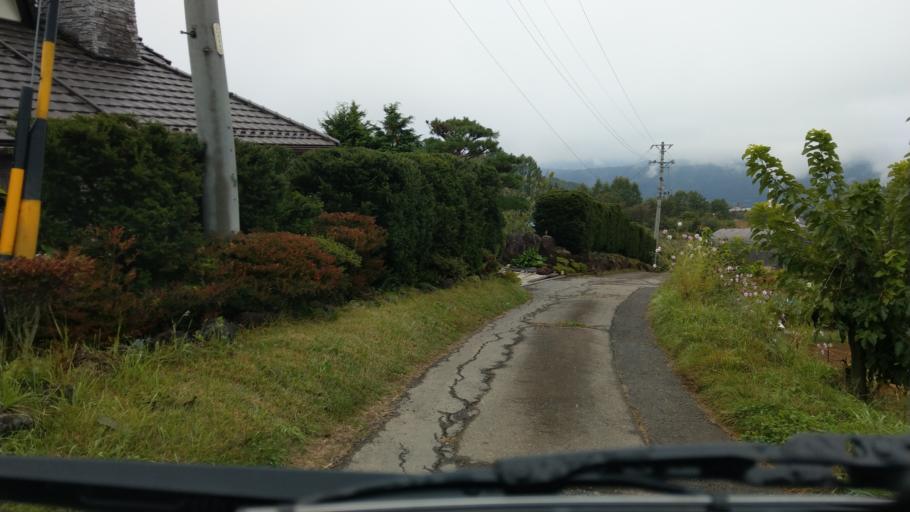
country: JP
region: Nagano
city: Komoro
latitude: 36.3577
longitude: 138.4447
